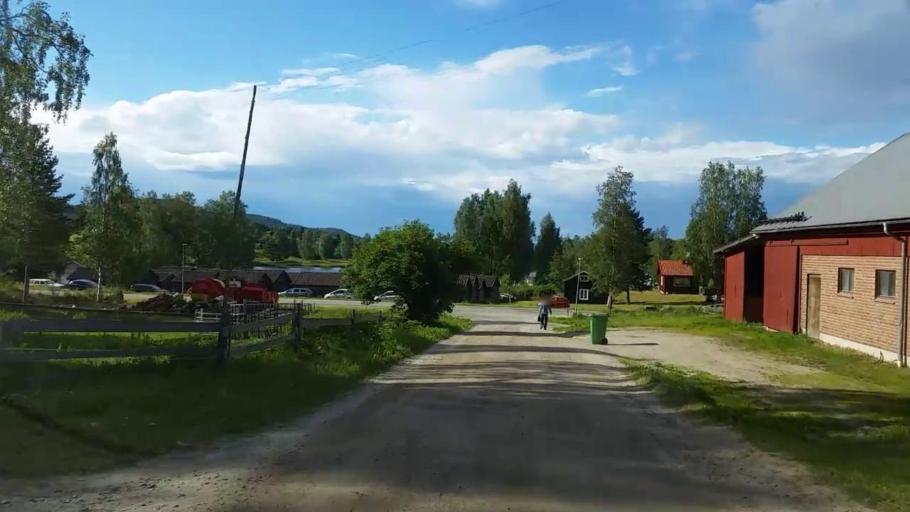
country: SE
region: Gaevleborg
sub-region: Ljusdals Kommun
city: Jaervsoe
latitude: 61.7097
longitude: 16.1890
